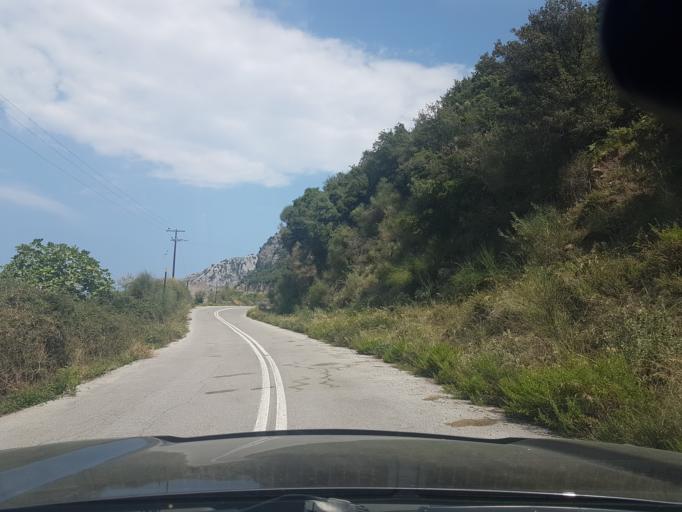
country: GR
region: Central Greece
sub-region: Nomos Evvoias
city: Kymi
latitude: 38.6432
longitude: 23.9603
